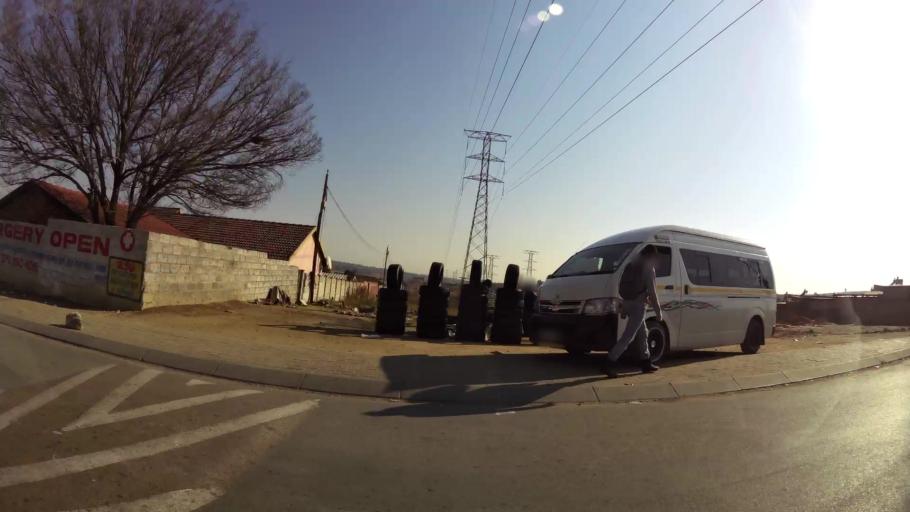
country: ZA
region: Gauteng
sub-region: City of Johannesburg Metropolitan Municipality
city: Modderfontein
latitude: -26.1037
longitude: 28.1127
